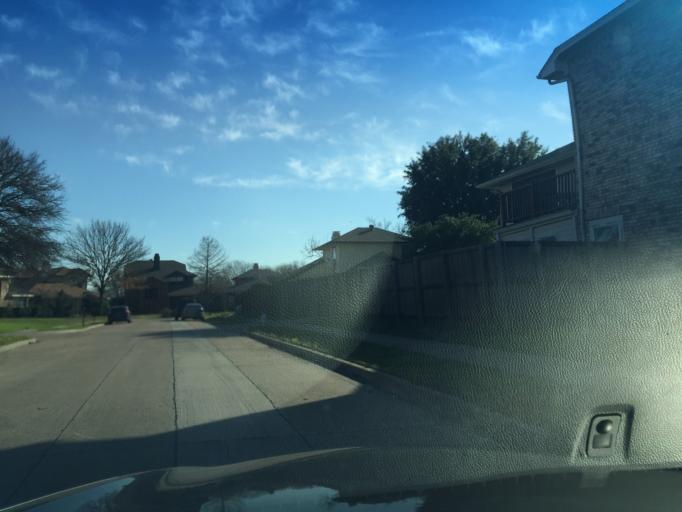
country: US
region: Texas
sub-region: Dallas County
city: Carrollton
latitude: 32.9972
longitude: -96.8981
